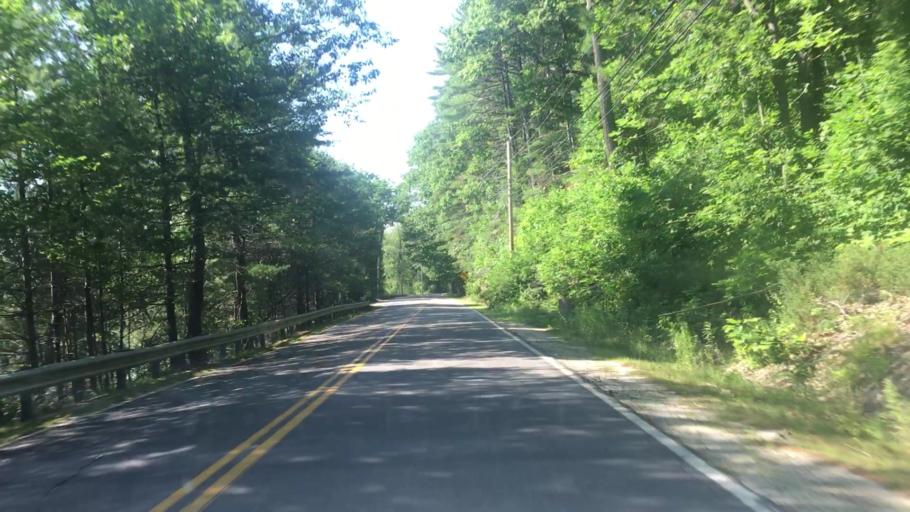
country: US
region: Maine
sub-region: York County
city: Hollis Center
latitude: 43.6619
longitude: -70.5979
